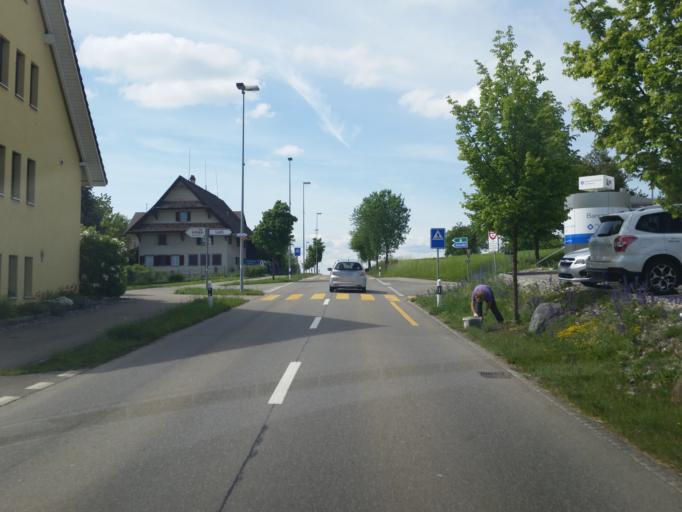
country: CH
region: Aargau
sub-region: Bezirk Bremgarten
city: Unterlunkhofen
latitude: 47.3366
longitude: 8.3864
